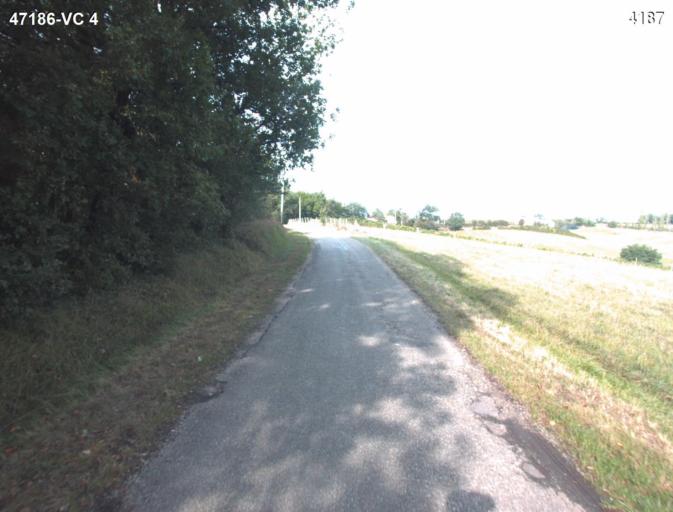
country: FR
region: Aquitaine
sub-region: Departement du Lot-et-Garonne
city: Sainte-Colombe-en-Bruilhois
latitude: 44.1954
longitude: 0.4493
